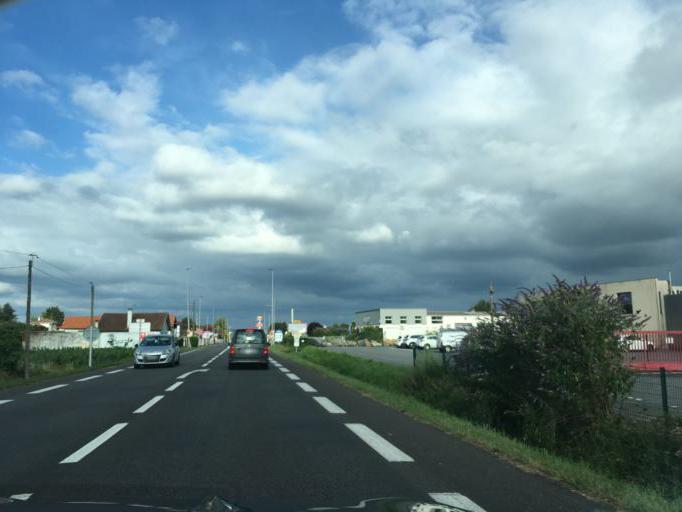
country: FR
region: Midi-Pyrenees
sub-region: Departement des Hautes-Pyrenees
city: Ibos
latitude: 43.2394
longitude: 0.0283
